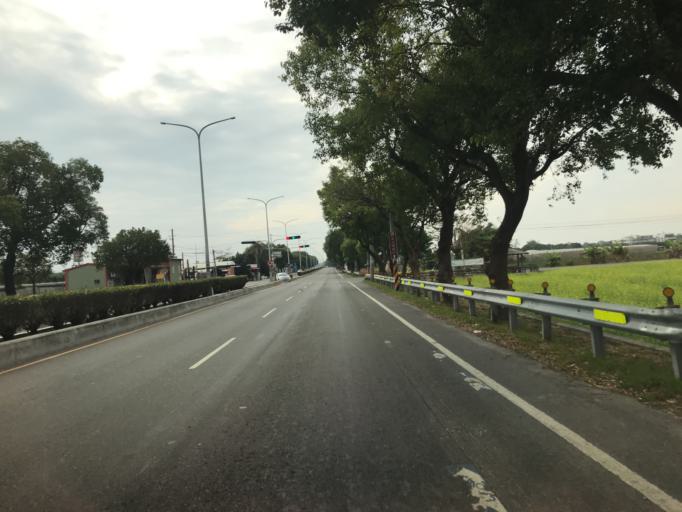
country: TW
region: Taiwan
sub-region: Yunlin
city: Douliu
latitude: 23.7673
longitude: 120.6208
